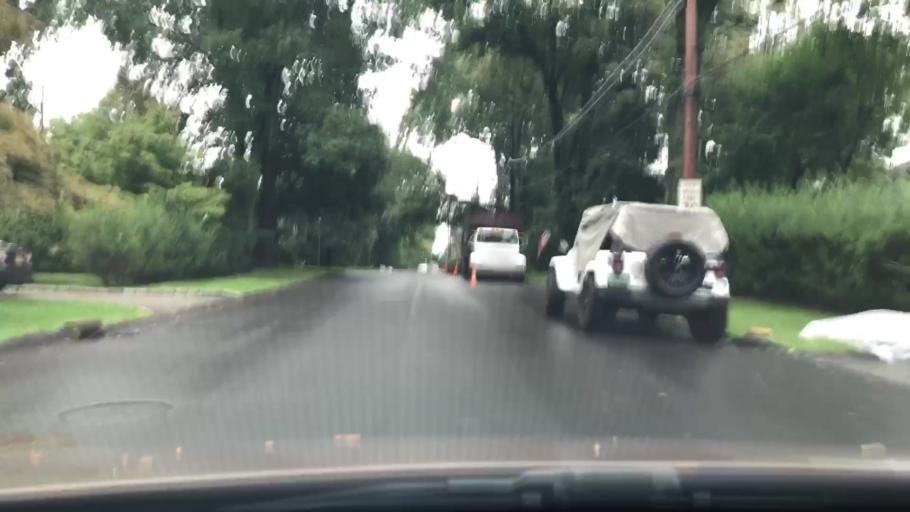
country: US
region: New York
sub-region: Westchester County
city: Scarsdale
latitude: 41.0086
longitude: -73.7711
